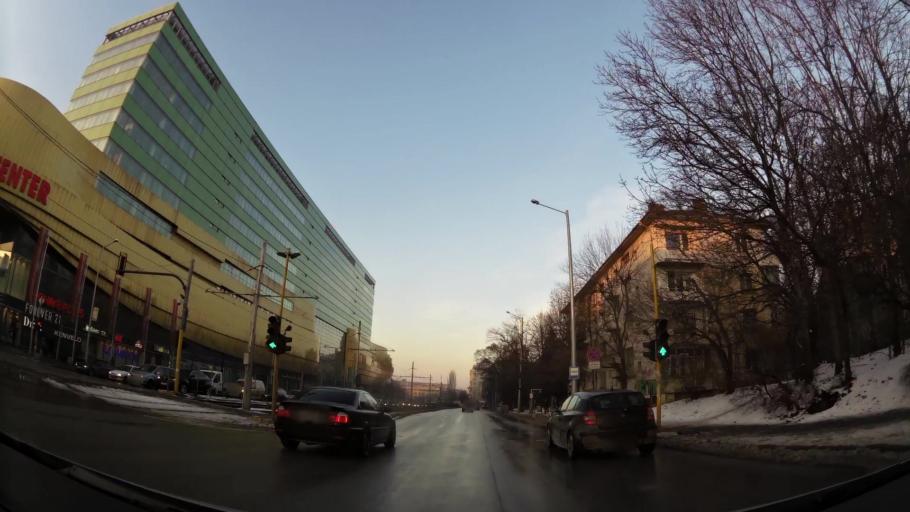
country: BG
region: Sofia-Capital
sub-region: Stolichna Obshtina
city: Sofia
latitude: 42.6905
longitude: 23.3543
